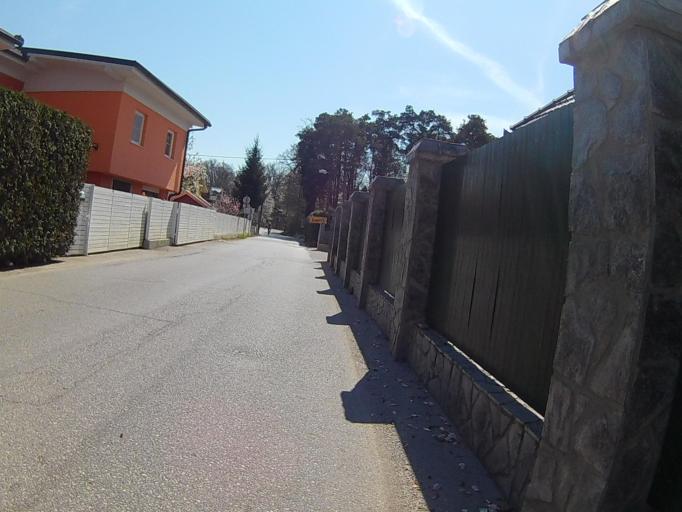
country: SI
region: Hoce-Slivnica
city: Rogoza
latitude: 46.4950
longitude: 15.6847
